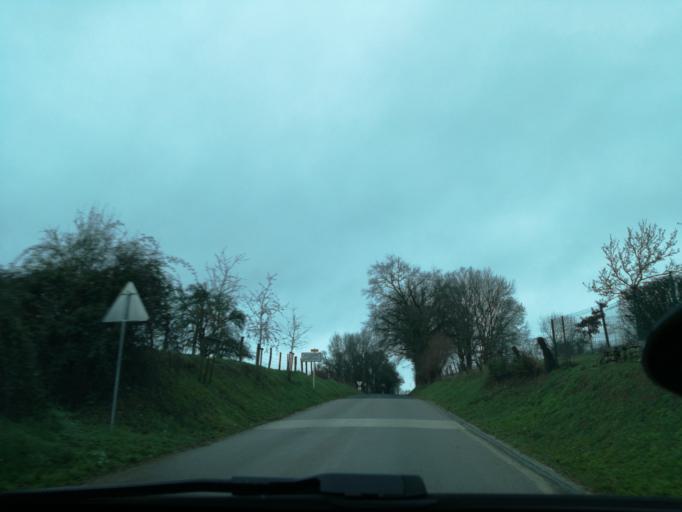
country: FR
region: Lorraine
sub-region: Departement de la Meuse
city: Revigny-sur-Ornain
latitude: 48.8859
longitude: 5.0783
